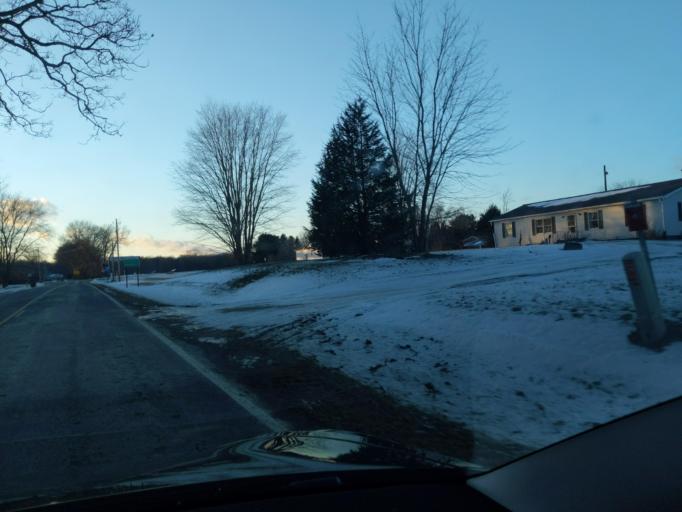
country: US
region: Michigan
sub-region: Ingham County
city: Stockbridge
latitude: 42.4502
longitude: -84.2564
